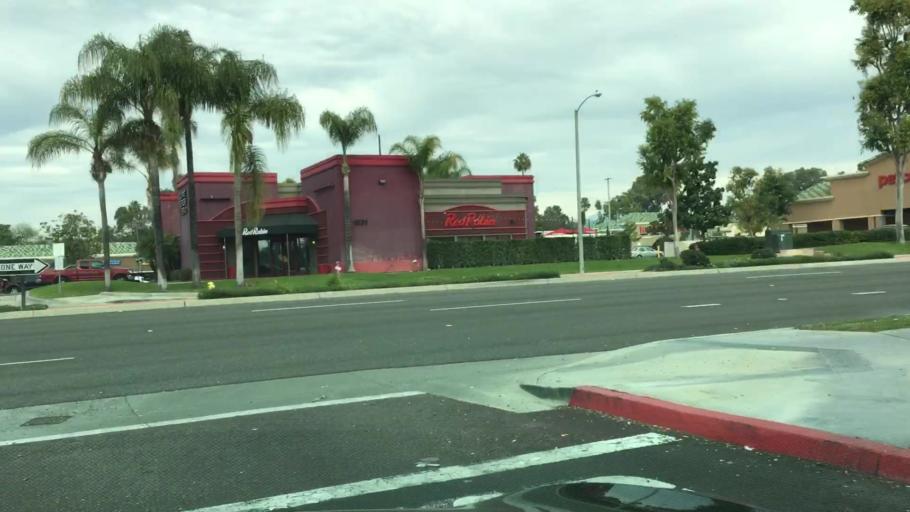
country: US
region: California
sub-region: Orange County
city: La Habra
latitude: 33.9171
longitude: -117.9642
